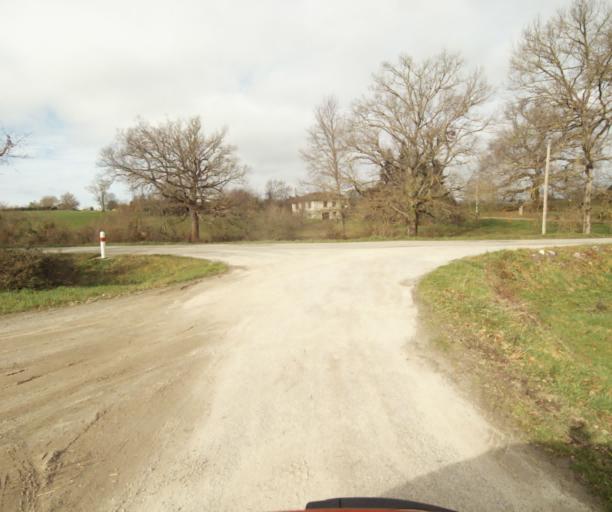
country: FR
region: Midi-Pyrenees
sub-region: Departement de l'Ariege
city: Pamiers
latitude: 43.0978
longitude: 1.5542
